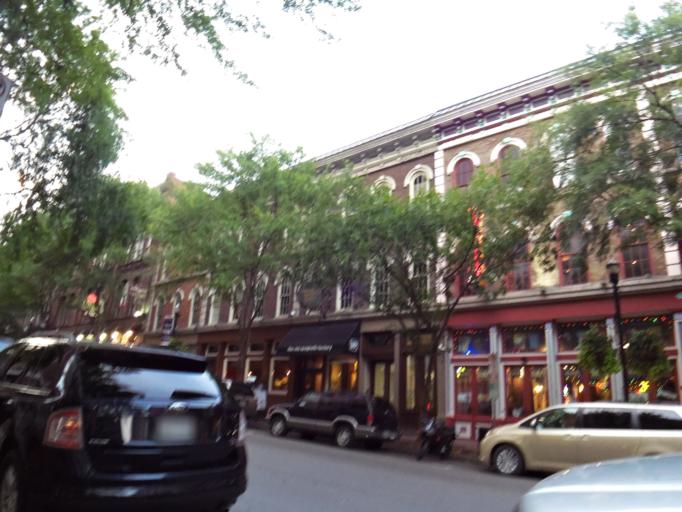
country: US
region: Tennessee
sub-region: Davidson County
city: Nashville
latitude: 36.1634
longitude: -86.7762
